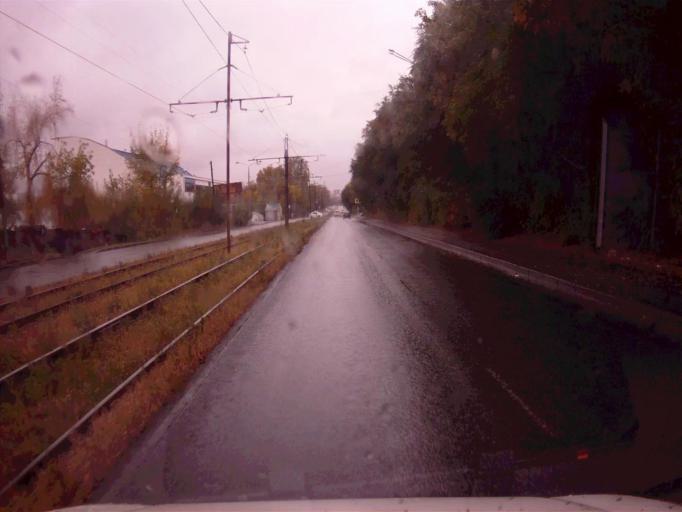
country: RU
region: Chelyabinsk
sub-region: Gorod Chelyabinsk
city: Chelyabinsk
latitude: 55.1765
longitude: 61.4150
